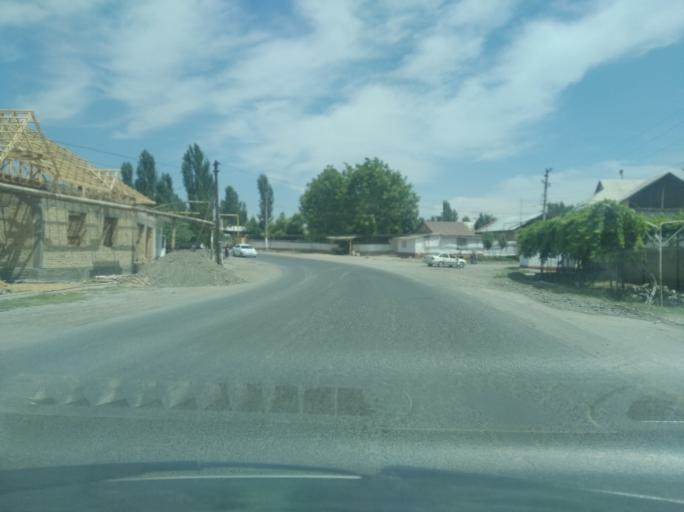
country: UZ
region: Andijon
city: Khujaobod
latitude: 40.6283
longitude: 72.4514
